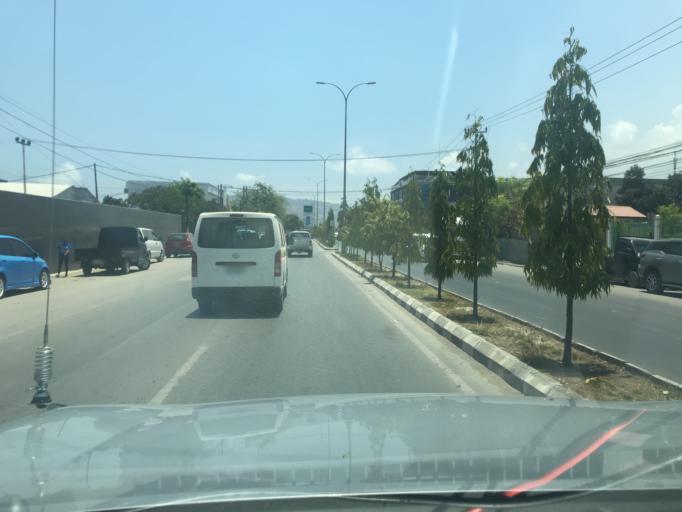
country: TL
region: Dili
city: Dili
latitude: -8.5540
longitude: 125.5580
